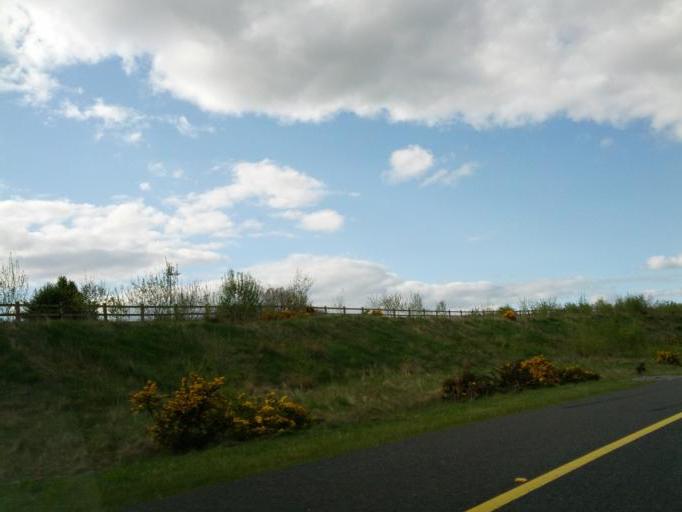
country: IE
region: Leinster
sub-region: An Iarmhi
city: Athlone
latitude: 53.3604
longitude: -8.0633
